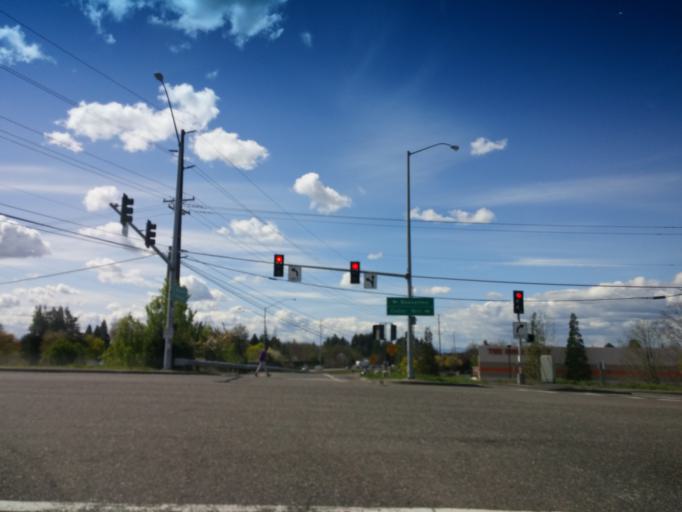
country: US
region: Oregon
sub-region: Washington County
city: Cedar Mill
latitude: 45.5230
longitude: -122.8154
